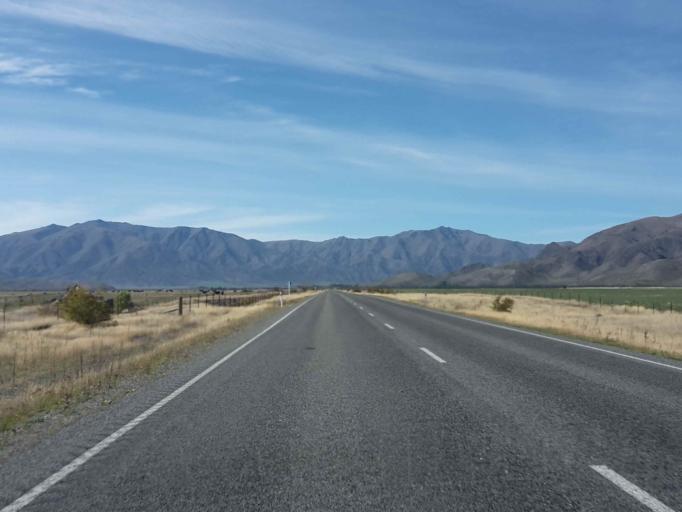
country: NZ
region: Otago
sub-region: Queenstown-Lakes District
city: Wanaka
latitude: -44.5044
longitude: 169.8802
